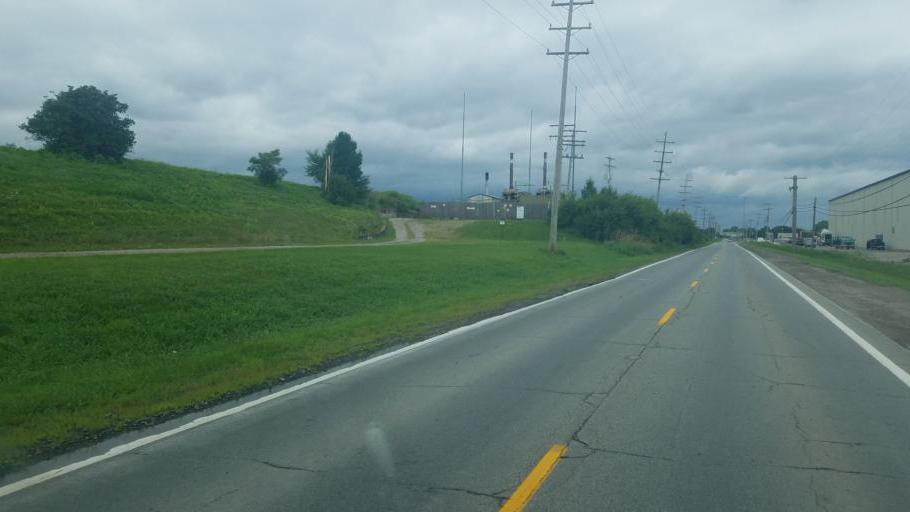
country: US
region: Ohio
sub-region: Franklin County
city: Grove City
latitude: 39.8910
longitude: -83.0273
